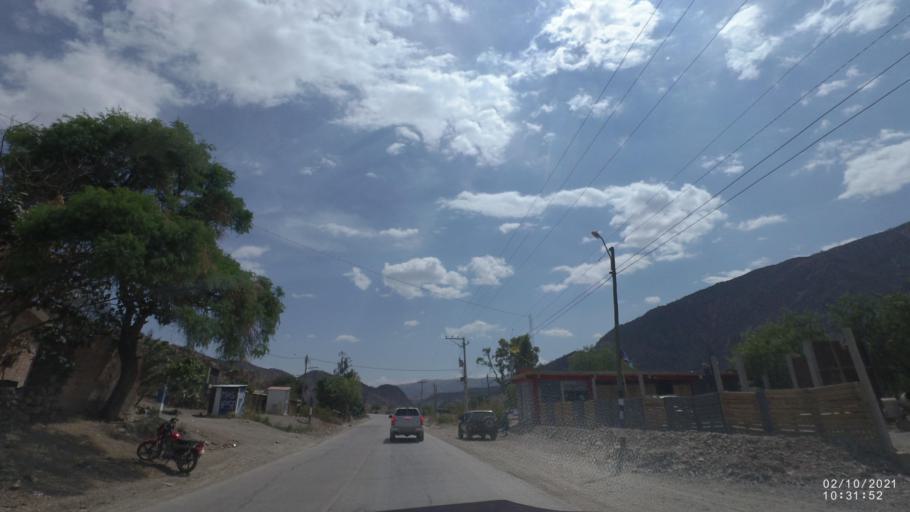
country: BO
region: Cochabamba
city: Capinota
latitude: -17.6926
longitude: -66.2578
